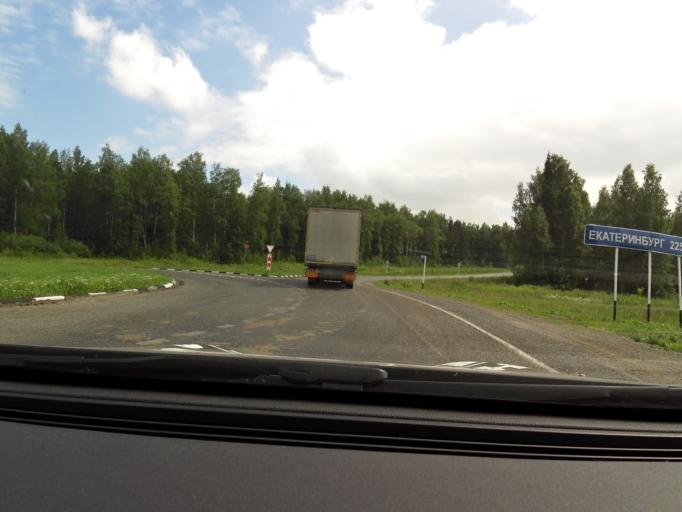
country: RU
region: Perm
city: Suksun
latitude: 57.0923
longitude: 57.3914
